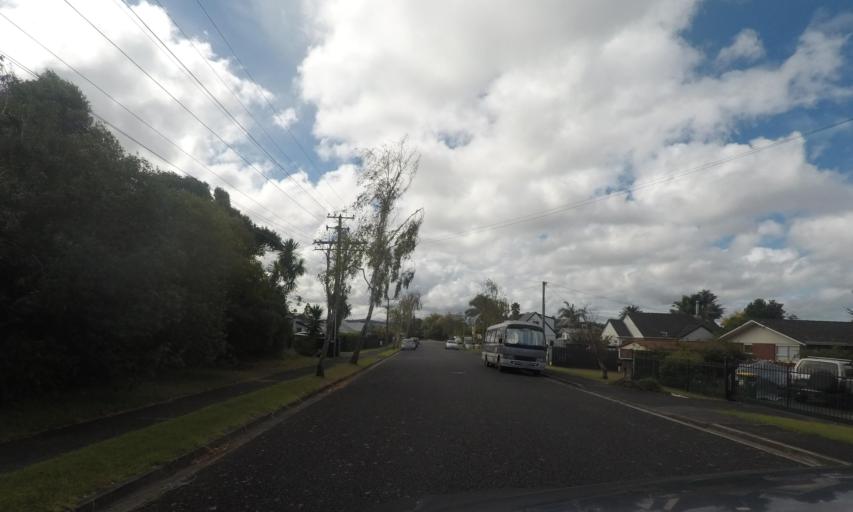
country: NZ
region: Auckland
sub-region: Auckland
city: Rosebank
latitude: -36.7799
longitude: 174.6444
